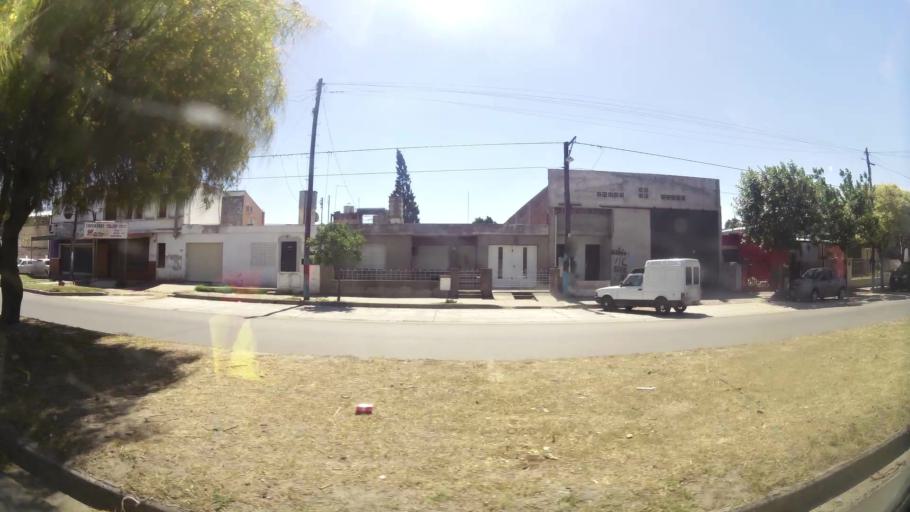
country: AR
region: Cordoba
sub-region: Departamento de Capital
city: Cordoba
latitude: -31.3692
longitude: -64.1494
